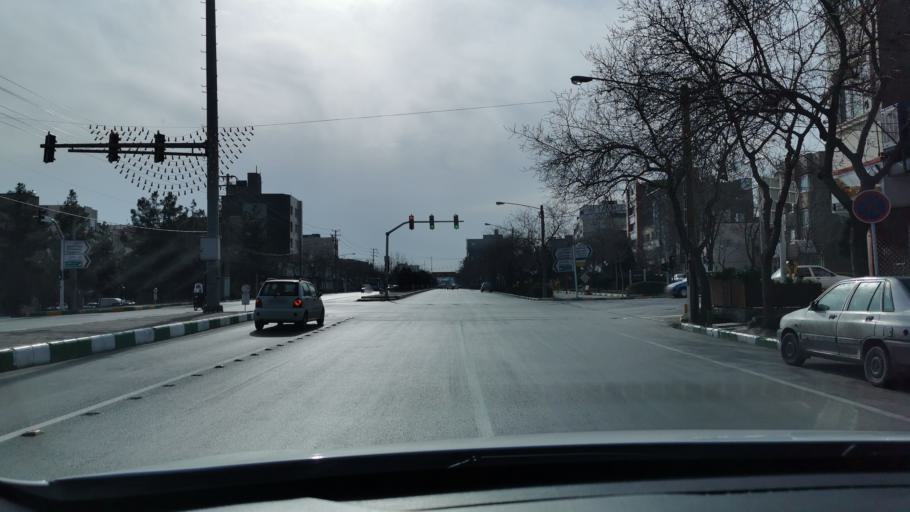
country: IR
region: Razavi Khorasan
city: Mashhad
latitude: 36.2989
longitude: 59.5243
